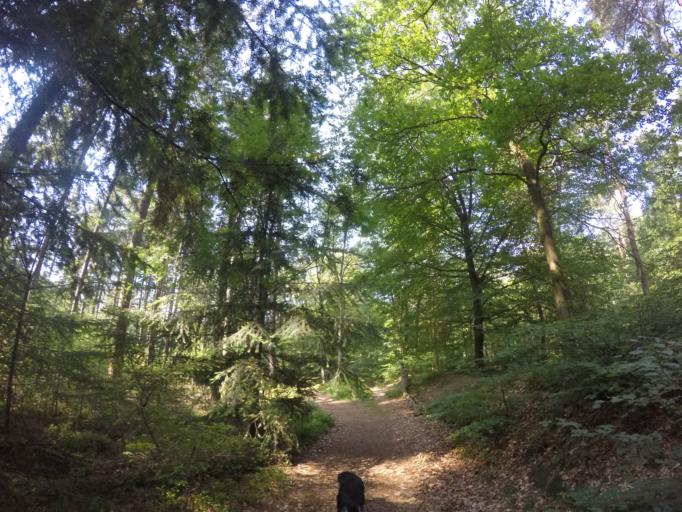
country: NL
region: Gelderland
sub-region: Gemeente Rozendaal
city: Rozendaal
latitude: 52.0189
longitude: 5.9812
